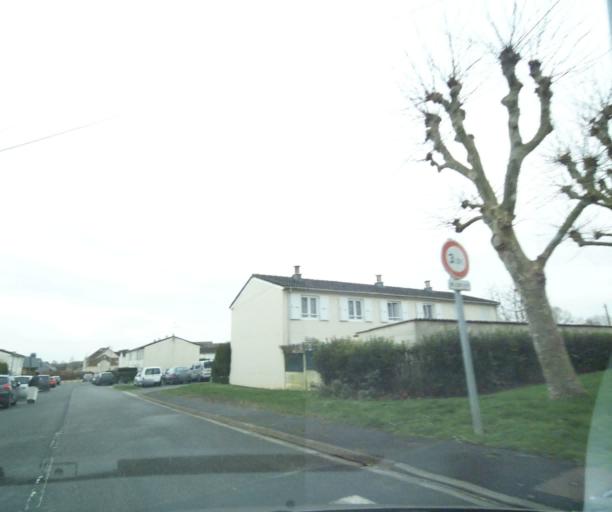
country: FR
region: Picardie
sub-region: Departement de l'Oise
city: Noyon
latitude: 49.5775
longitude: 2.9876
